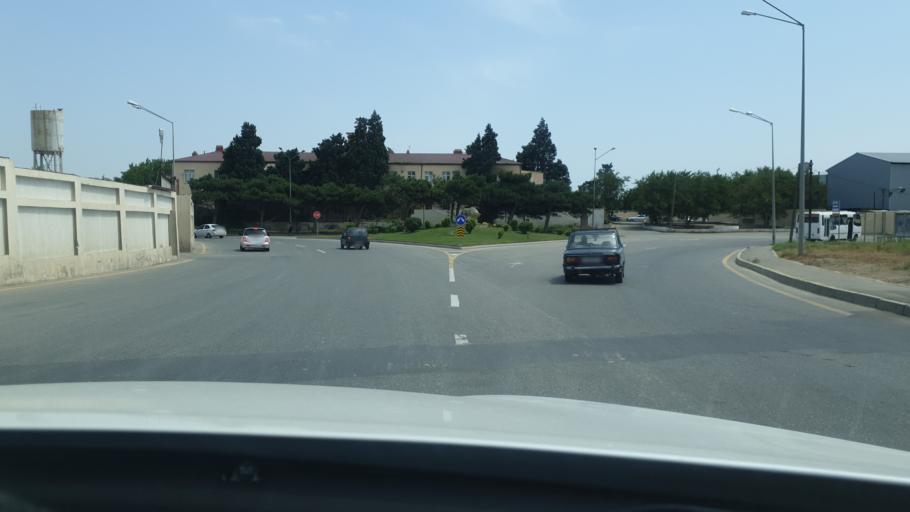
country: AZ
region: Baki
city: Qaracuxur
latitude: 40.3947
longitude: 49.9970
